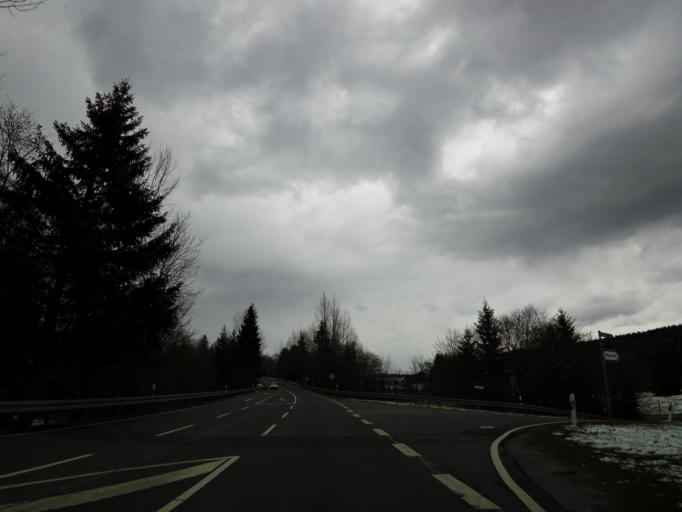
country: DE
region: Lower Saxony
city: Clausthal-Zellerfeld
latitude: 51.7708
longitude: 10.3197
